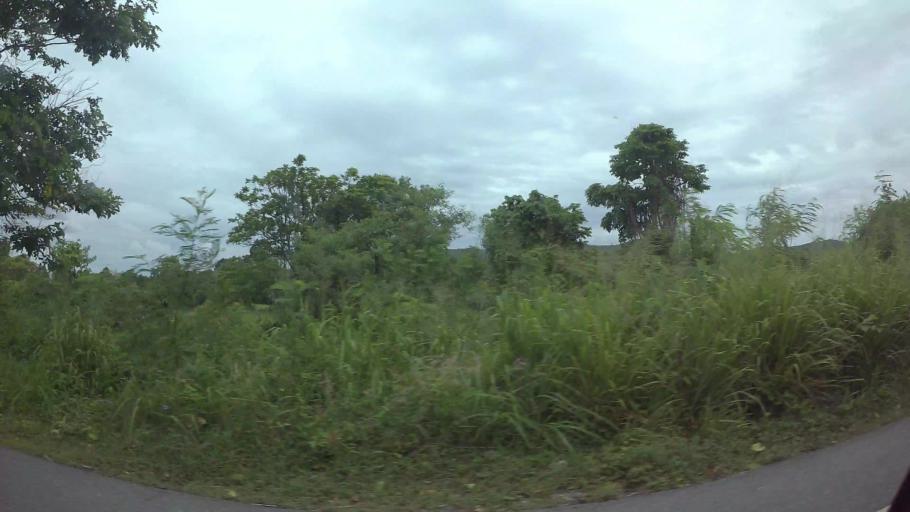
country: TH
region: Chon Buri
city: Si Racha
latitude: 13.1805
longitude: 100.9747
